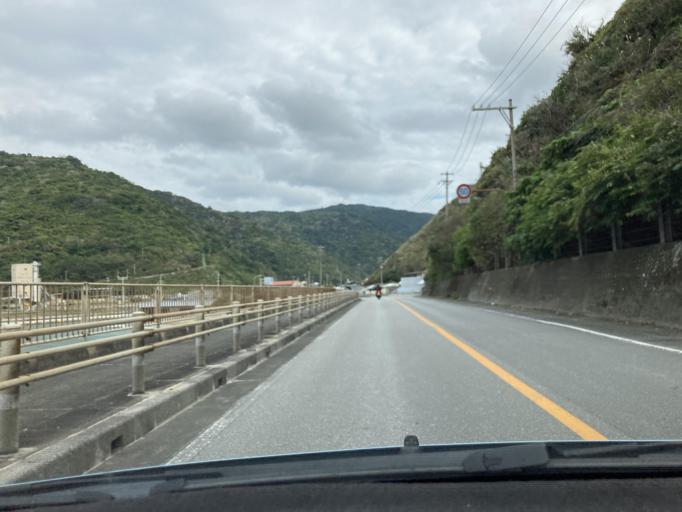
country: JP
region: Okinawa
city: Nago
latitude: 26.7972
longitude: 128.2301
